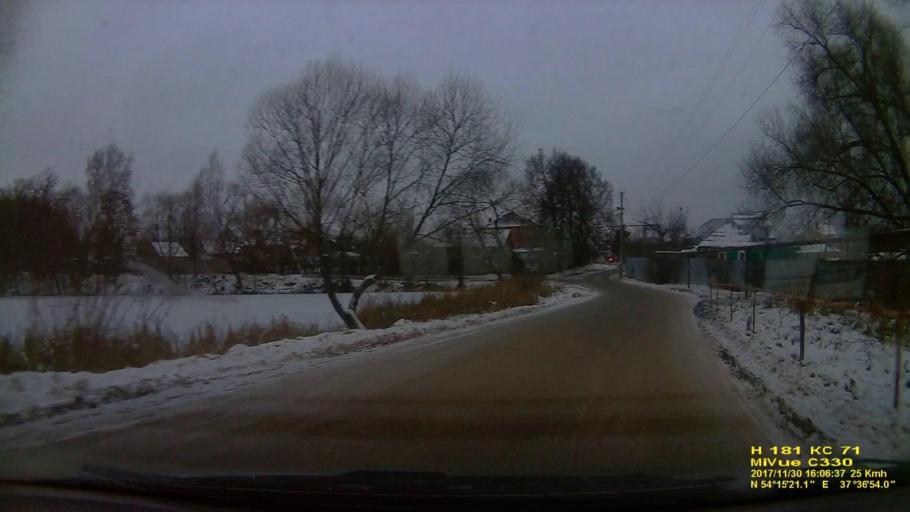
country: RU
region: Tula
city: Gorelki
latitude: 54.2558
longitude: 37.6145
